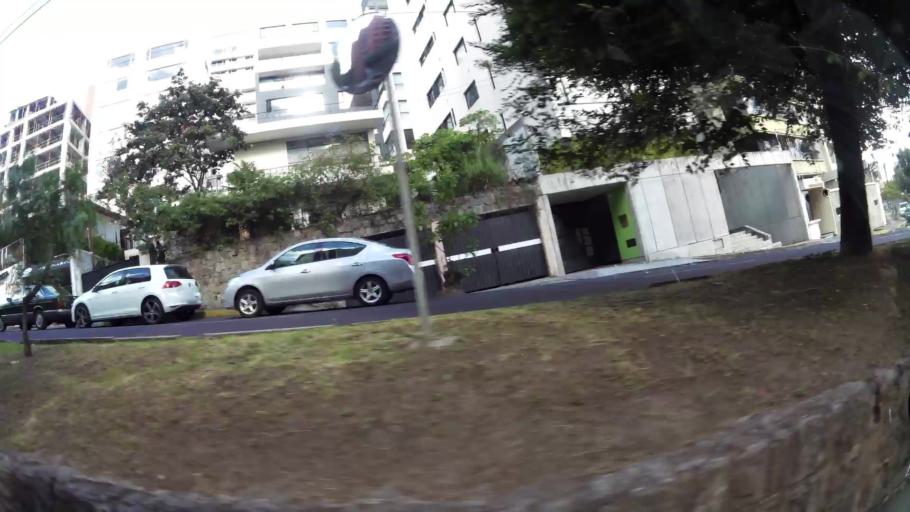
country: EC
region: Pichincha
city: Quito
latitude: -0.1945
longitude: -78.4792
